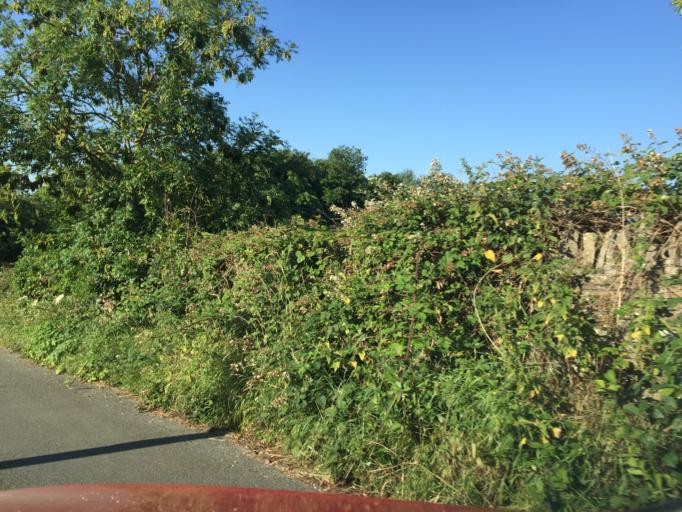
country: GB
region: England
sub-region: South Gloucestershire
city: Winterbourne
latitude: 51.5096
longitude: -2.5091
